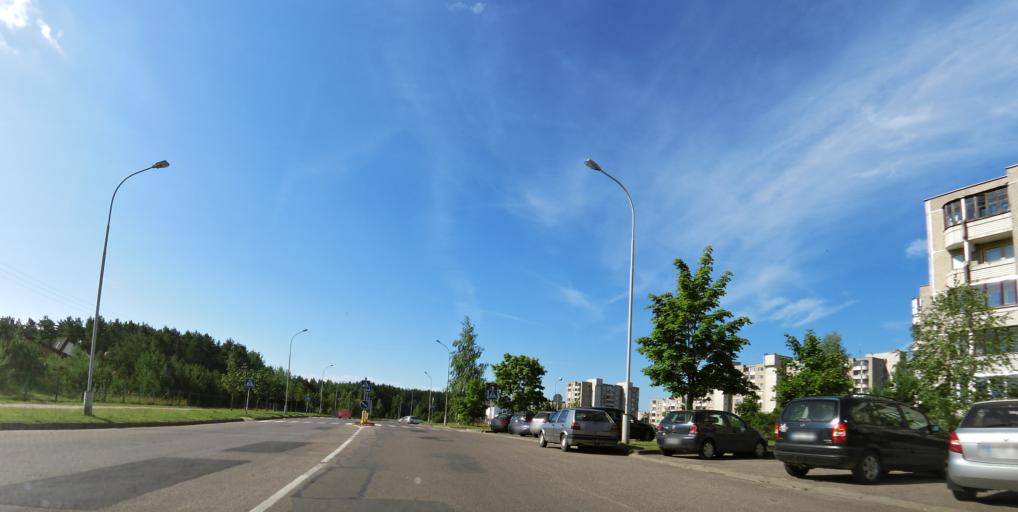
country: LT
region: Vilnius County
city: Pilaite
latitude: 54.7051
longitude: 25.1887
